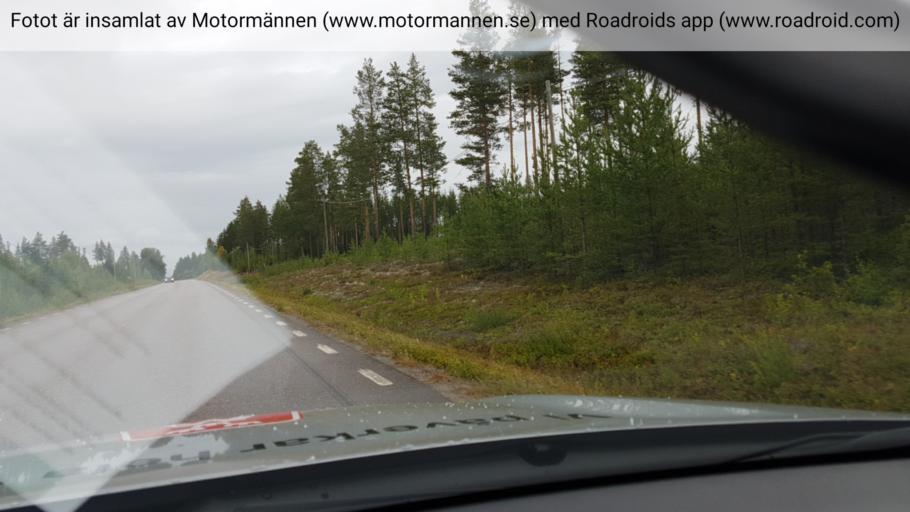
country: SE
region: Norrbotten
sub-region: Alvsbyns Kommun
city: AElvsbyn
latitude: 66.1051
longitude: 20.9361
